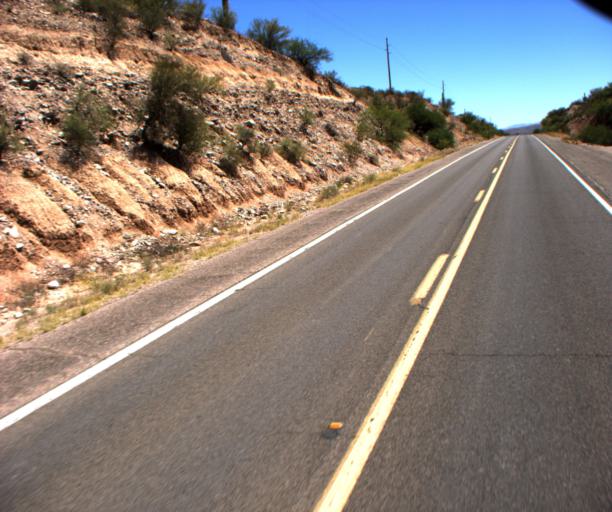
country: US
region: Arizona
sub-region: Pinal County
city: Mammoth
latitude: 32.8958
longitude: -110.7168
